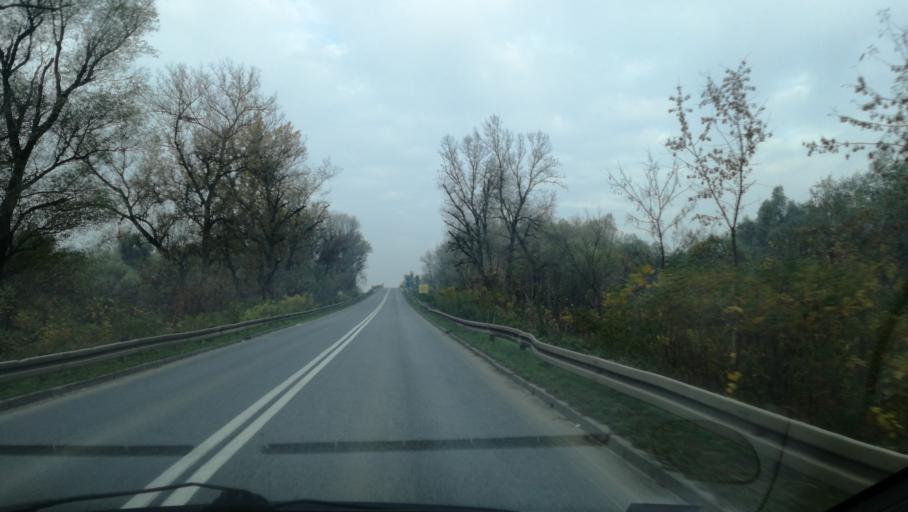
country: RS
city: Taras
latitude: 45.3956
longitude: 20.2168
